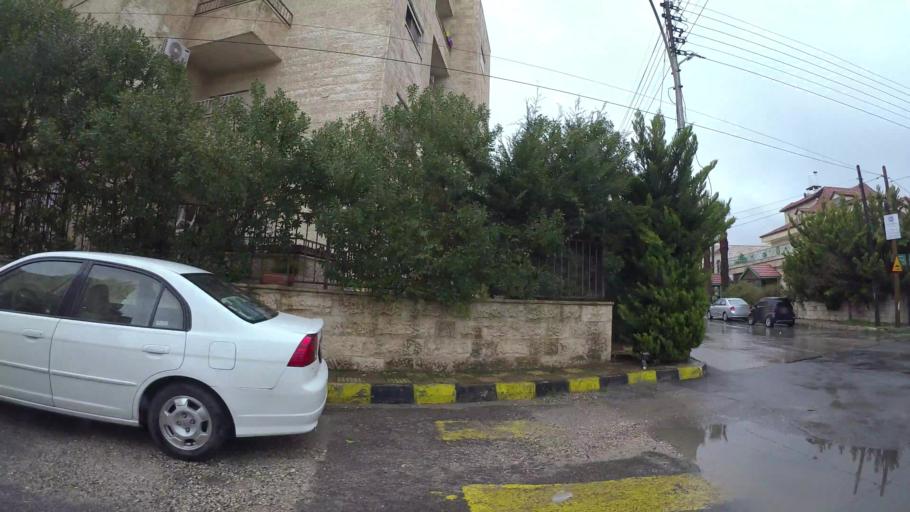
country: JO
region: Amman
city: Wadi as Sir
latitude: 31.9680
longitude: 35.8626
